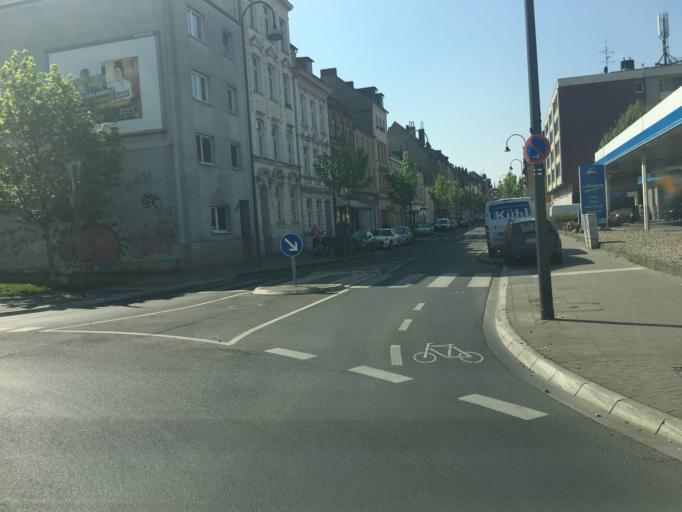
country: DE
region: North Rhine-Westphalia
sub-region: Regierungsbezirk Koln
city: Muelheim
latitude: 50.9741
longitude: 7.0127
